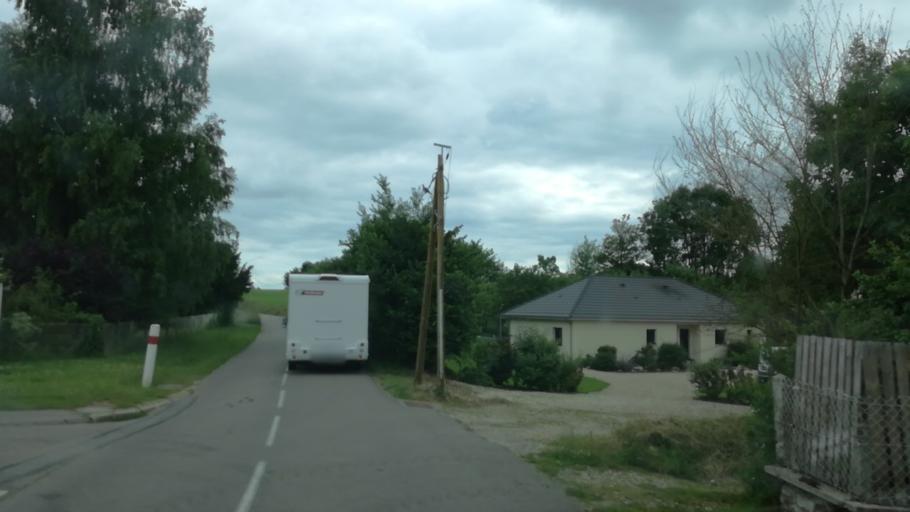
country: FR
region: Haute-Normandie
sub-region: Departement de l'Eure
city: Bourg-Achard
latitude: 49.3321
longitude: 0.8115
